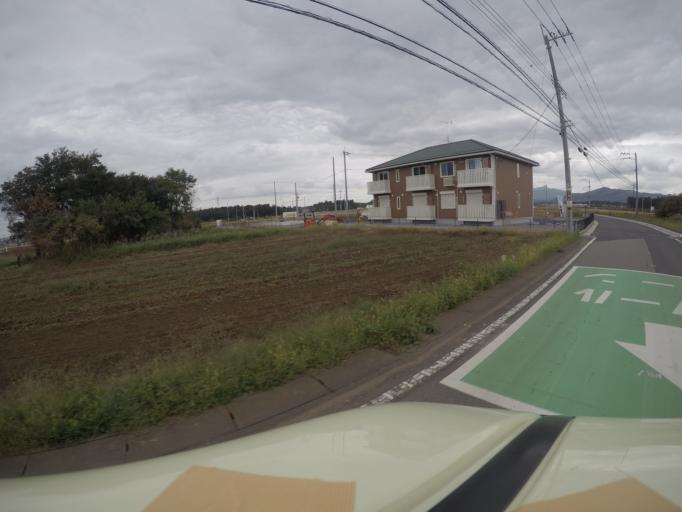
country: JP
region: Ibaraki
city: Naka
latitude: 36.0986
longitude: 140.1248
